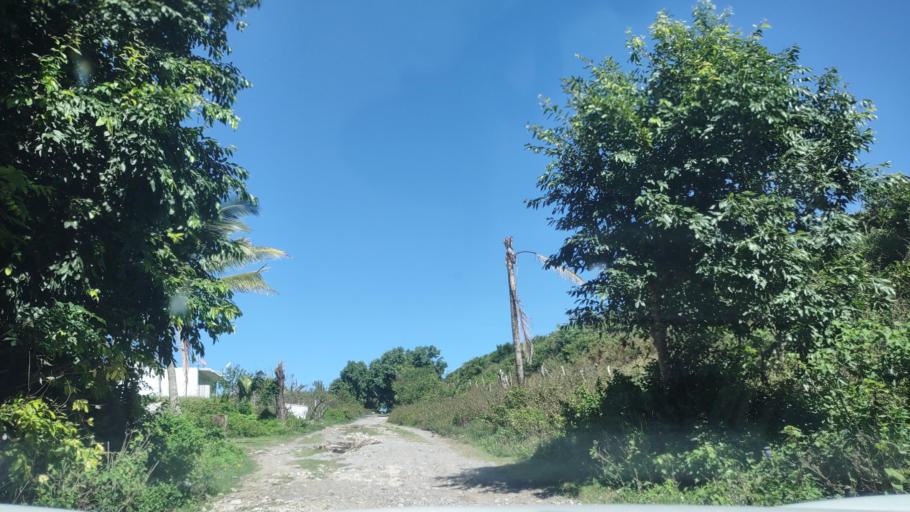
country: MX
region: Veracruz
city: Heroica Alvarado
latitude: 18.7847
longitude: -95.7691
